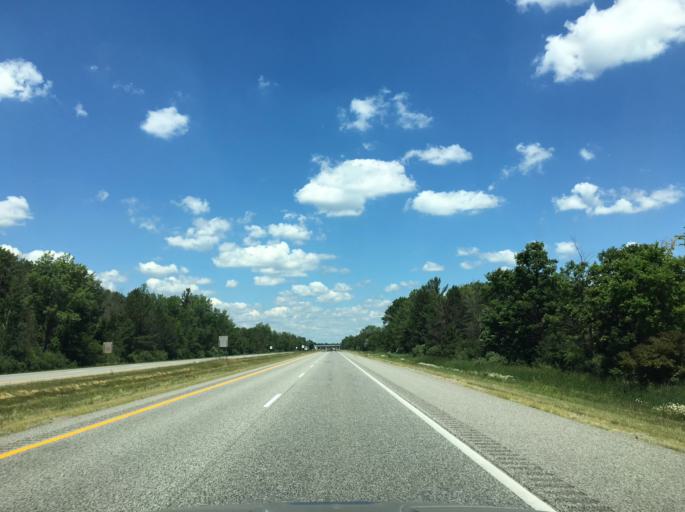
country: US
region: Michigan
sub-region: Midland County
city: Midland
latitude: 43.6316
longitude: -84.1805
